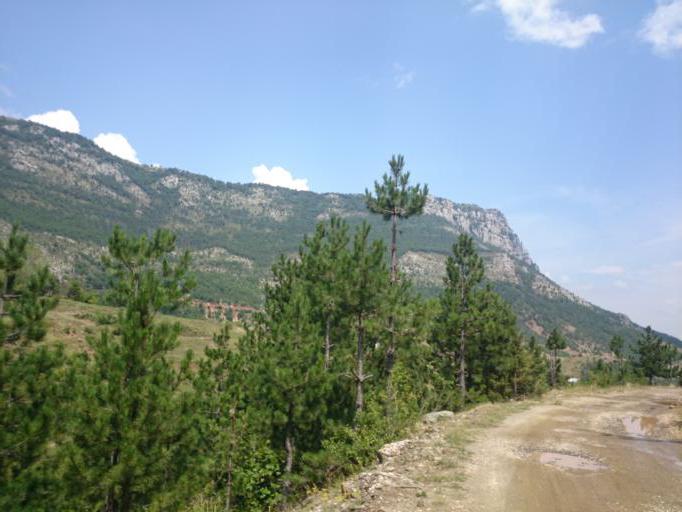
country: AL
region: Diber
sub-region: Rrethi i Dibres
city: Fushe-Lure
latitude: 41.8317
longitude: 20.1819
